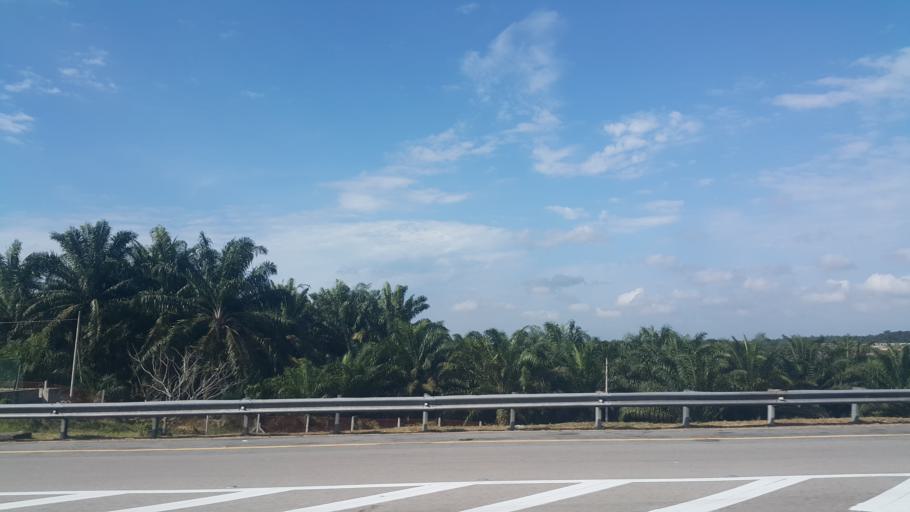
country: MY
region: Johor
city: Kampung Simpang Renggam
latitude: 1.7667
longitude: 103.3514
